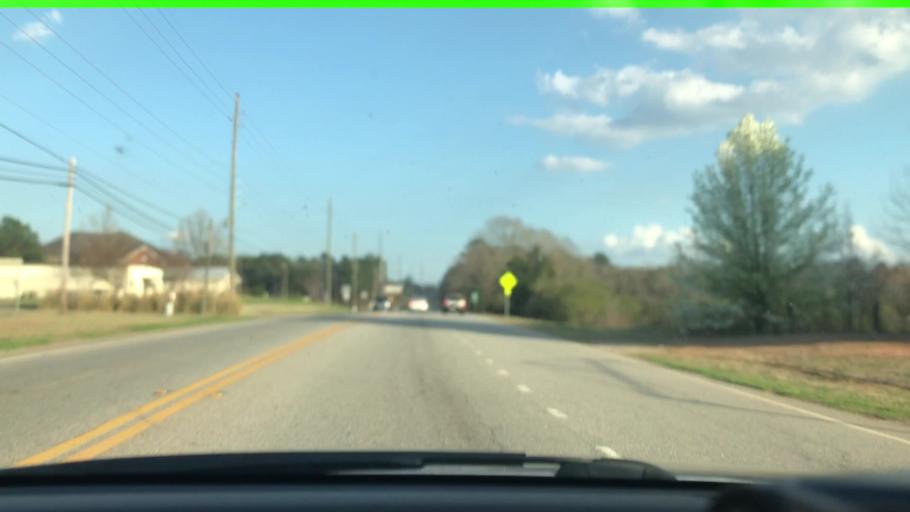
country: US
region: Georgia
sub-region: Oglethorpe County
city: Lexington
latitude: 33.8890
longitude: -83.1339
